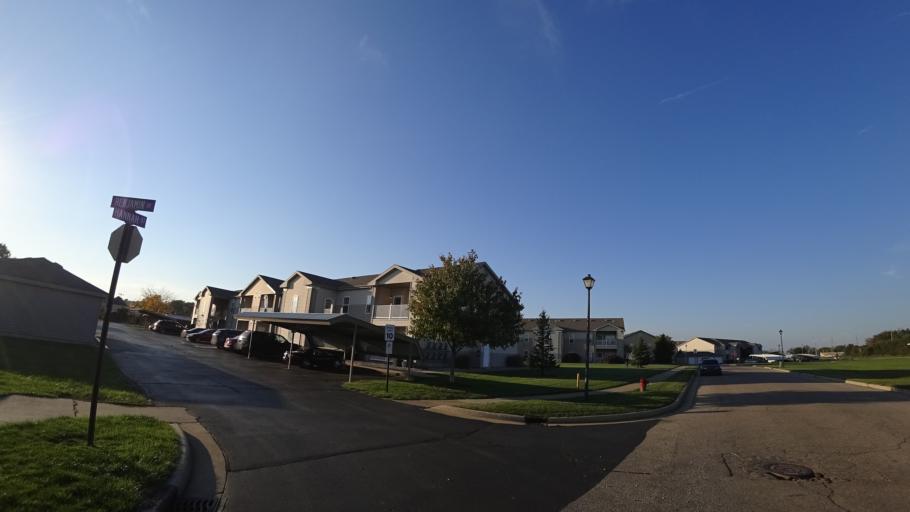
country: US
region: Michigan
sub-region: Saint Joseph County
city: Three Rivers
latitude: 41.9440
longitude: -85.6470
